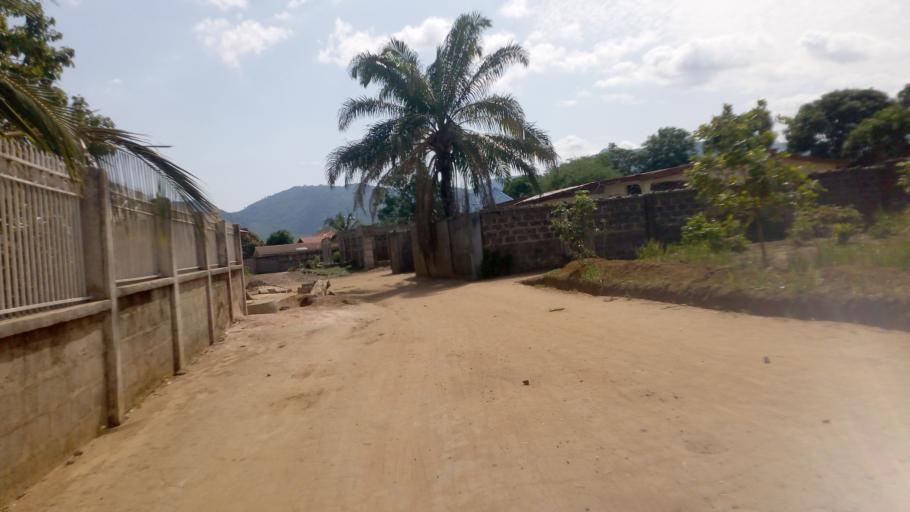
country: SL
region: Western Area
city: Waterloo
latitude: 8.3188
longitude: -13.0755
